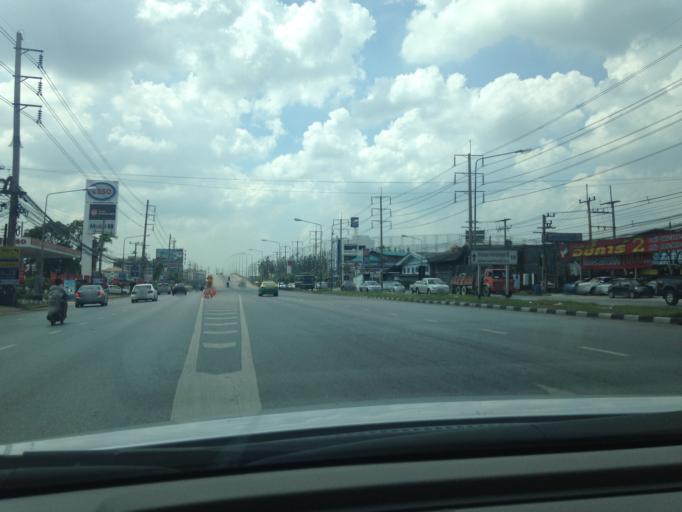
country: TH
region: Phra Nakhon Si Ayutthaya
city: Ban Bang Kadi Pathum Thani
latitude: 13.9850
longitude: 100.5964
